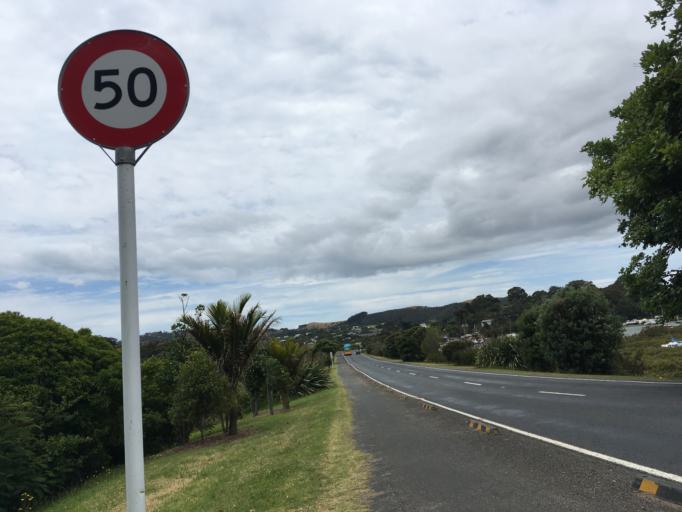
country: NZ
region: Auckland
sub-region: Auckland
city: Pakuranga
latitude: -36.7988
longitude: 175.0360
